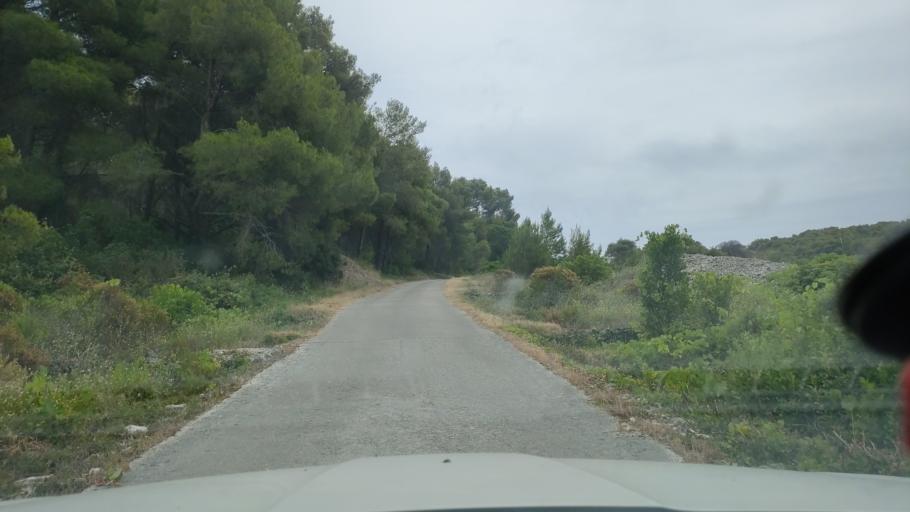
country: HR
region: Splitsko-Dalmatinska
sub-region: Grad Vis
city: Vis
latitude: 43.0307
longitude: 16.1678
